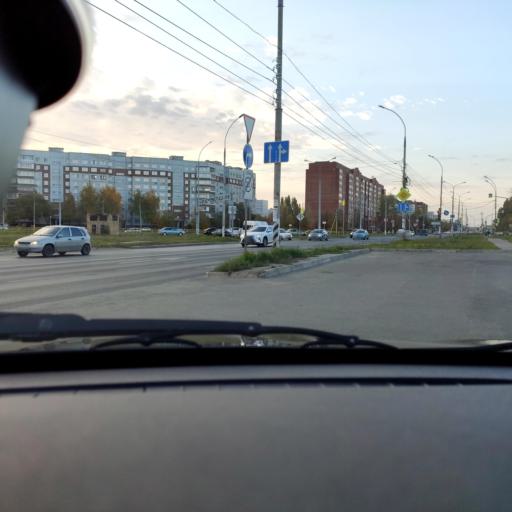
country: RU
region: Samara
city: Tol'yatti
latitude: 53.5437
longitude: 49.3159
